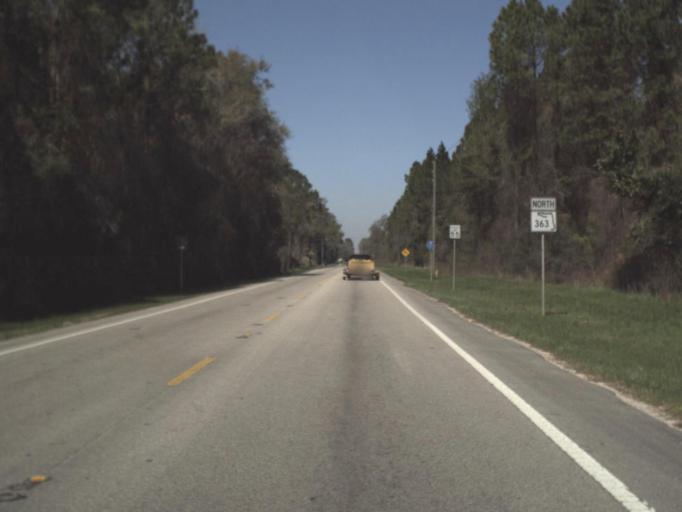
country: US
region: Florida
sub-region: Leon County
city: Woodville
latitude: 30.2380
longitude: -84.2312
